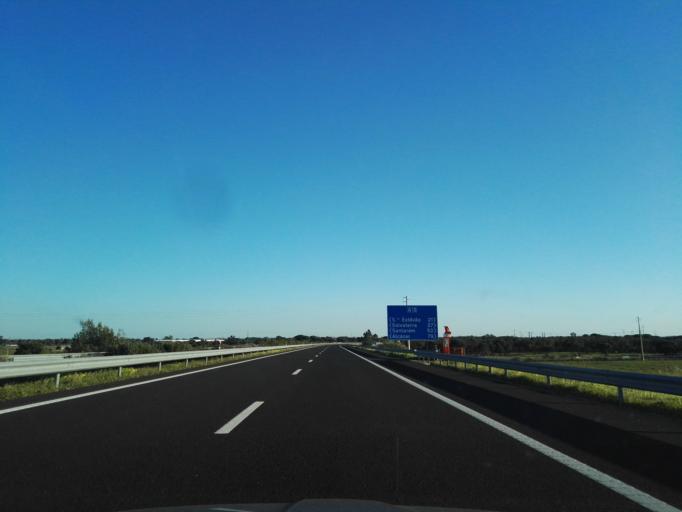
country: PT
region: Santarem
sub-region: Benavente
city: Benavente
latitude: 38.9502
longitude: -8.8236
